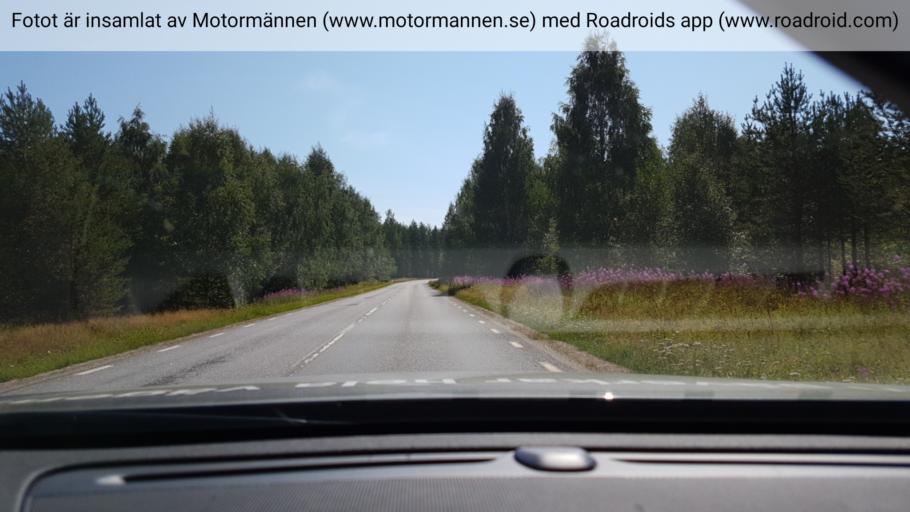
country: SE
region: Vaesterbotten
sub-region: Vindelns Kommun
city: Vindeln
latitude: 64.2770
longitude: 19.6299
